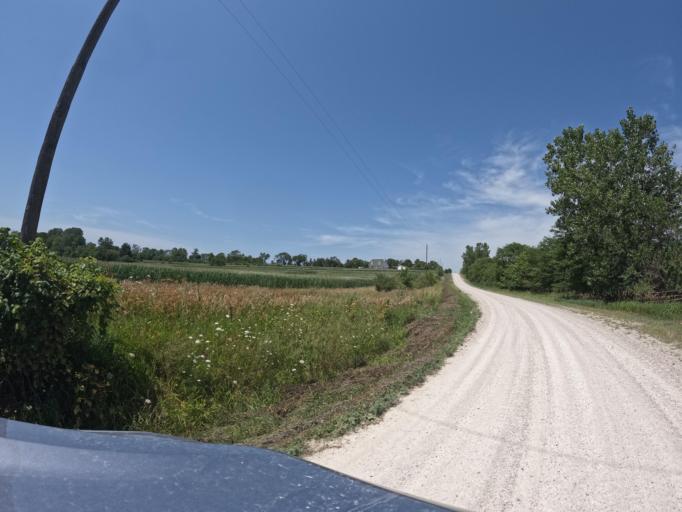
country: US
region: Iowa
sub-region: Henry County
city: Mount Pleasant
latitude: 40.9842
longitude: -91.6506
